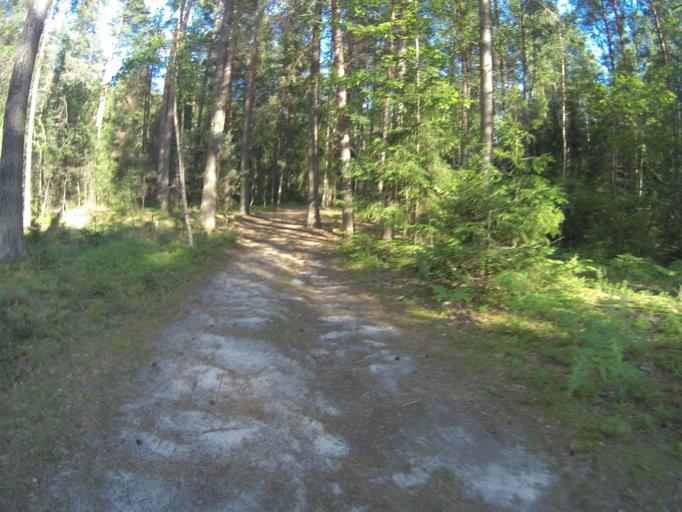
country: RU
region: Vladimir
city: Raduzhnyy
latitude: 56.0478
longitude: 40.2444
